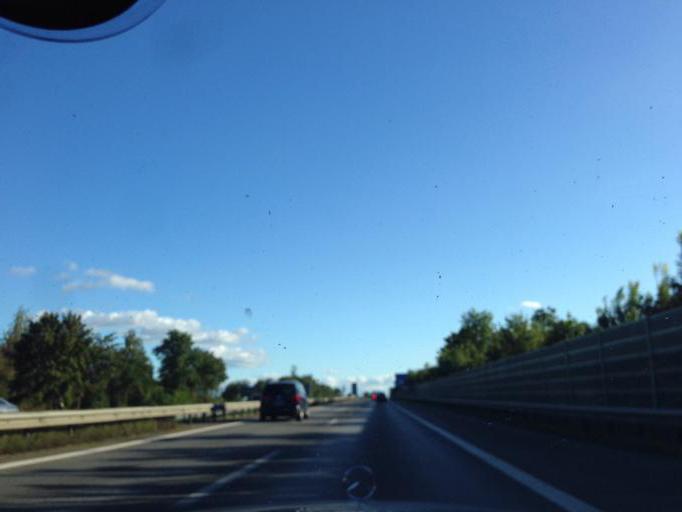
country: DE
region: Schleswig-Holstein
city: Padenstedt
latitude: 54.0504
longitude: 9.9266
